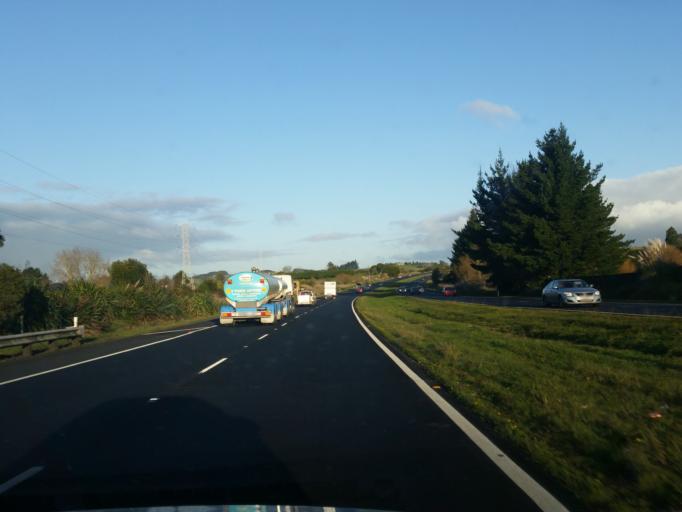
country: NZ
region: Auckland
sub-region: Auckland
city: Pukekohe East
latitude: -37.2421
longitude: 175.0237
